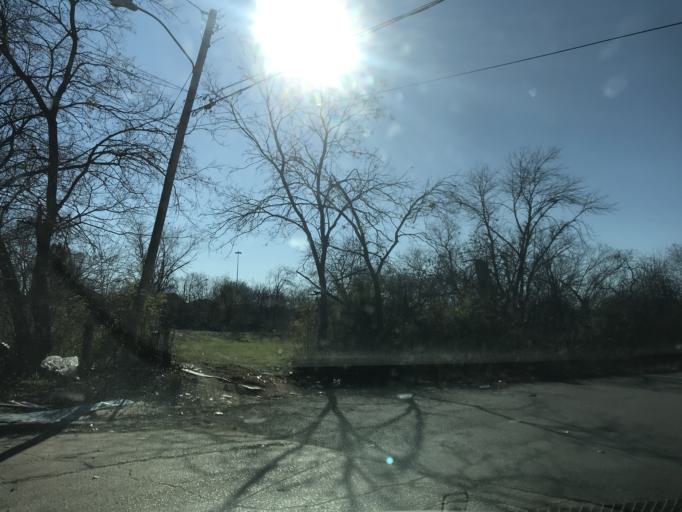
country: US
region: Texas
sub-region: Dallas County
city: Cockrell Hill
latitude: 32.7705
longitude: -96.9080
